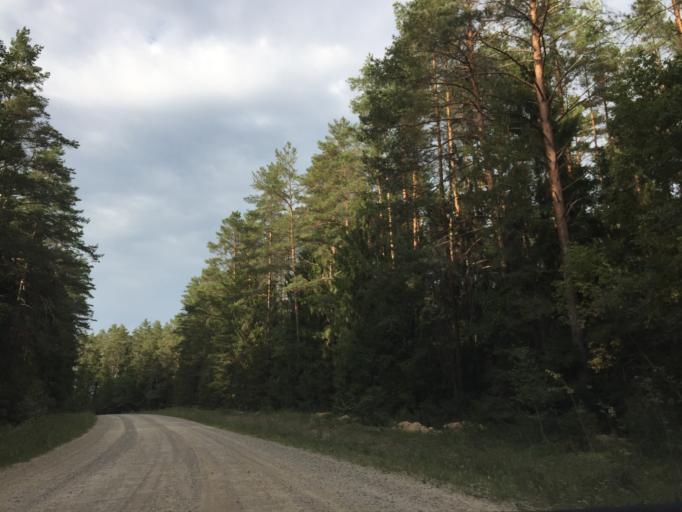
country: LV
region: Baldone
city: Baldone
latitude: 56.7872
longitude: 24.4433
